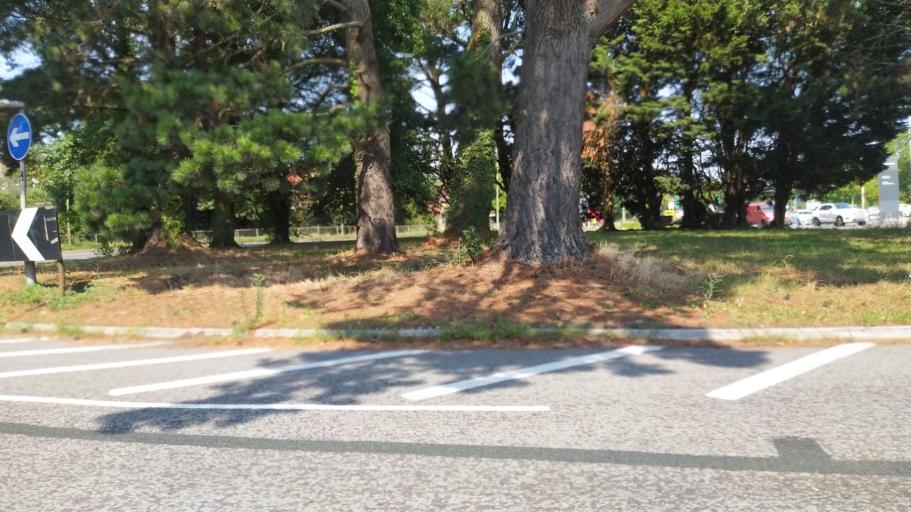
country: GB
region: England
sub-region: Hampshire
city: Totton
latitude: 50.9125
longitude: -1.4928
